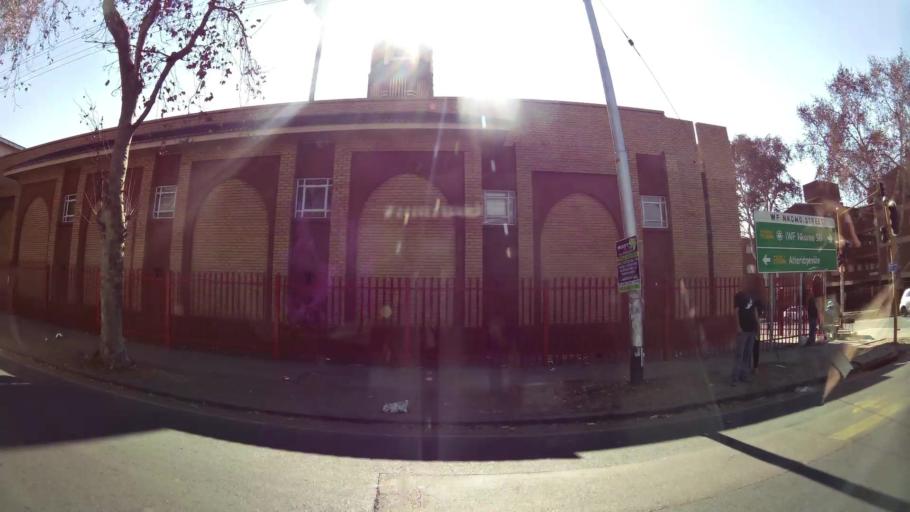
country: ZA
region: Gauteng
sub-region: City of Tshwane Metropolitan Municipality
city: Pretoria
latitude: -25.7482
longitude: 28.1621
